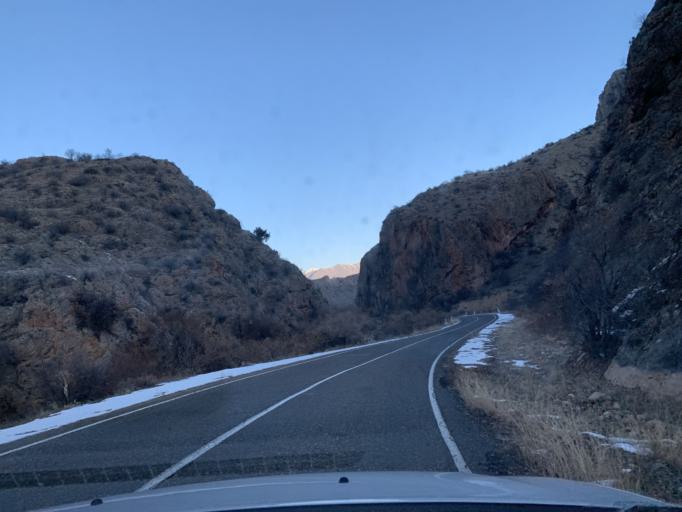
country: AM
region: Vayots' Dzori Marz
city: Areni
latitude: 39.6960
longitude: 45.2115
